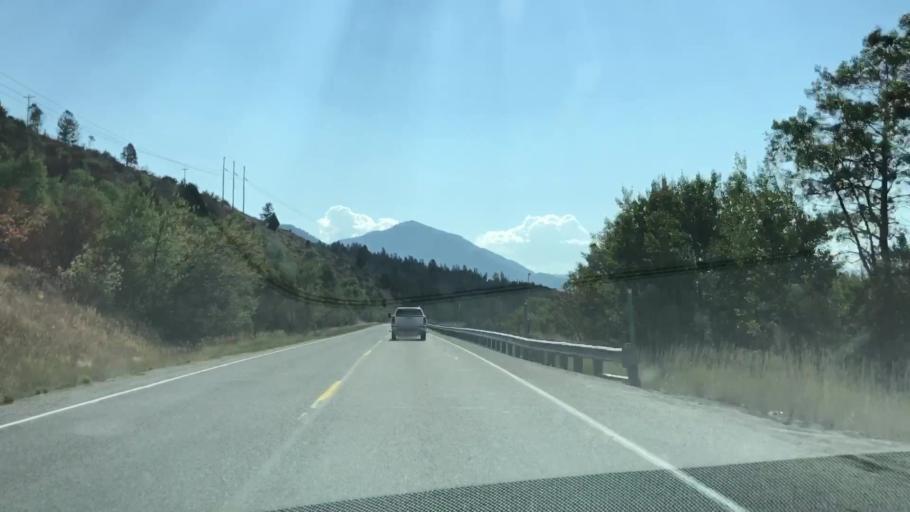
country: US
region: Wyoming
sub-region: Teton County
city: Hoback
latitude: 43.2053
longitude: -111.0505
